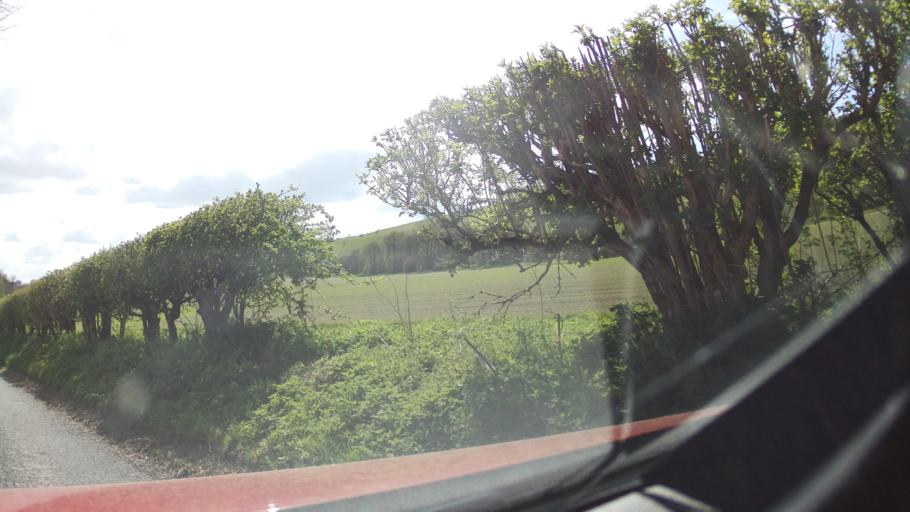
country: GB
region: England
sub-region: West Berkshire
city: Kintbury
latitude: 51.3427
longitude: -1.4707
